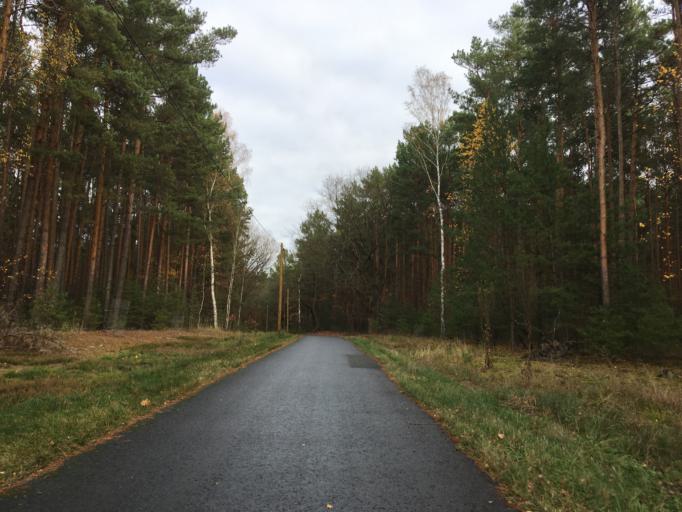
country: DE
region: Brandenburg
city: Tauer
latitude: 51.9118
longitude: 14.4645
